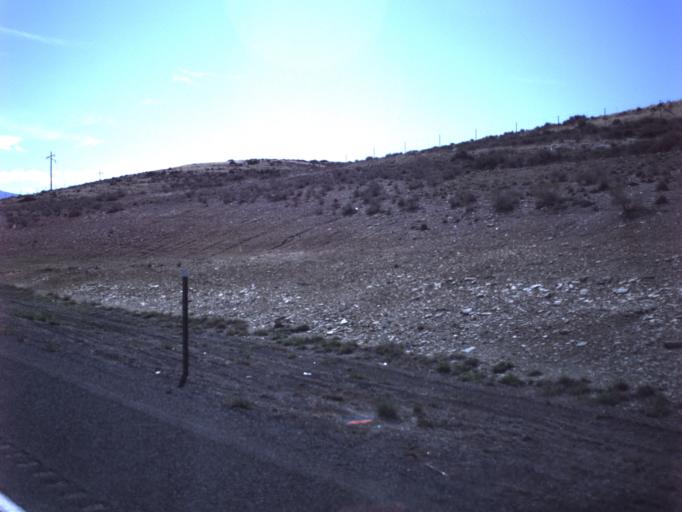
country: US
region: Utah
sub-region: Sanpete County
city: Gunnison
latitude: 39.1719
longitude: -111.8313
